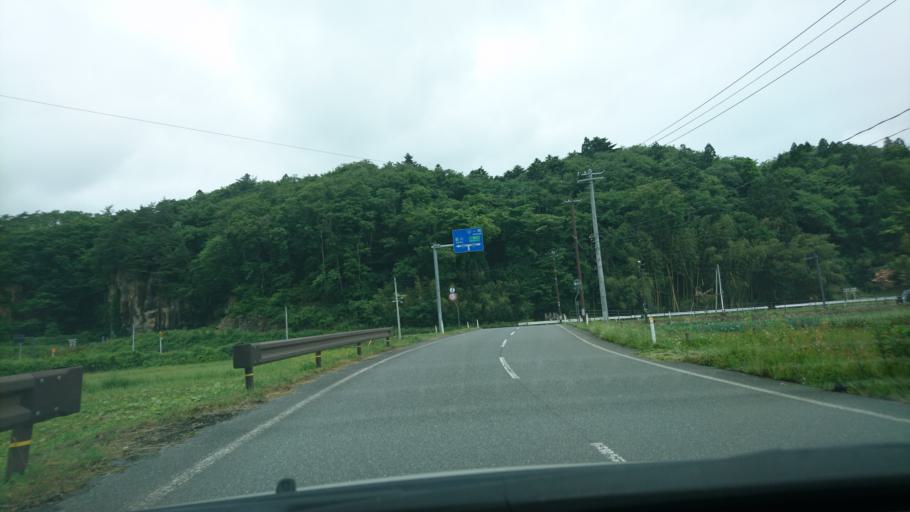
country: JP
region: Iwate
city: Ichinoseki
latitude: 38.9488
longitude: 141.0379
